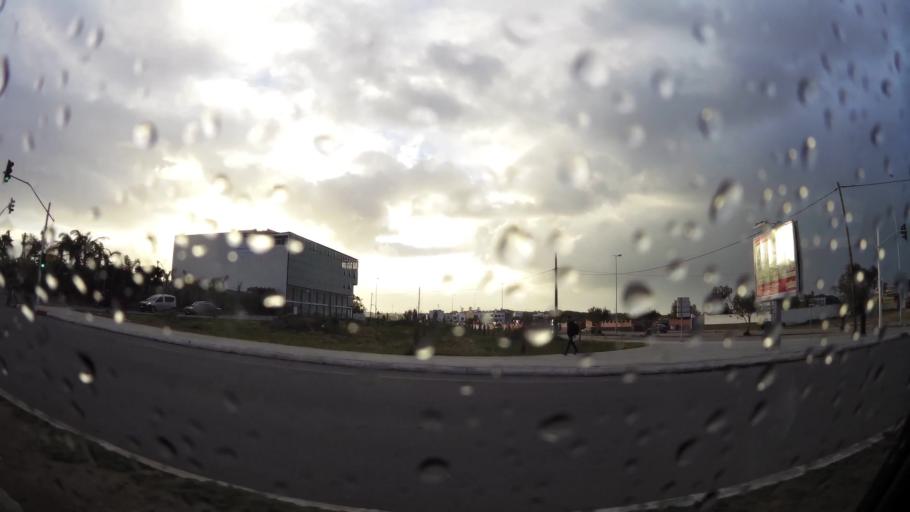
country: MA
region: Doukkala-Abda
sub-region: El-Jadida
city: El Jadida
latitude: 33.2368
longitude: -8.4828
